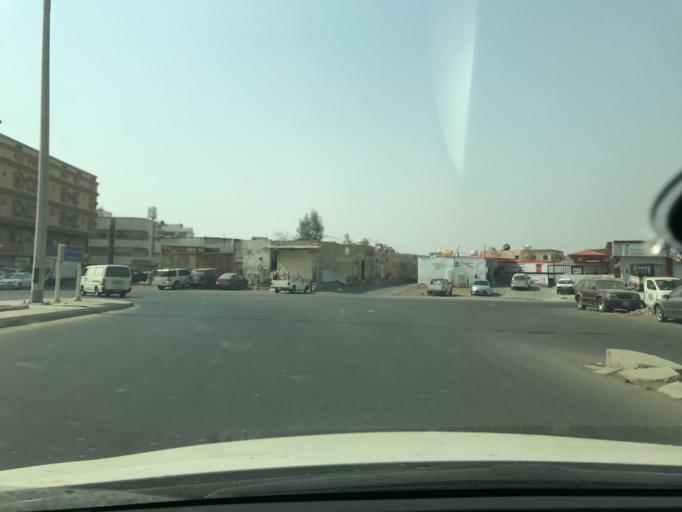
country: SA
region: Makkah
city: Jeddah
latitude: 21.6289
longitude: 39.1670
